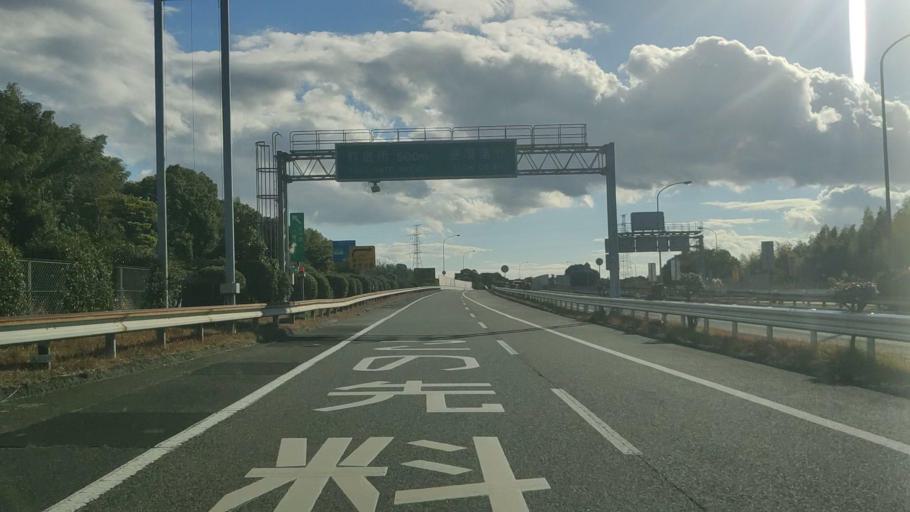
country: JP
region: Fukuoka
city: Nogata
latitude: 33.7862
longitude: 130.7462
